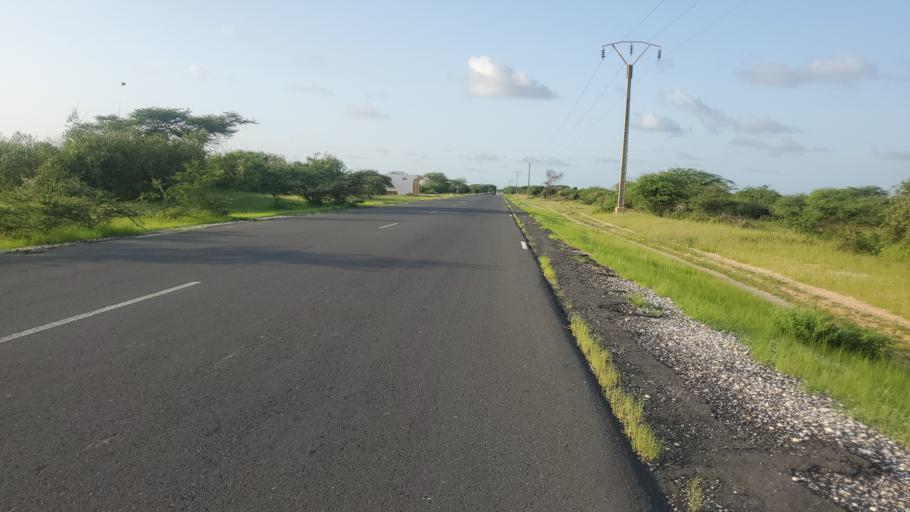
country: SN
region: Saint-Louis
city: Saint-Louis
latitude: 16.1794
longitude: -16.4095
